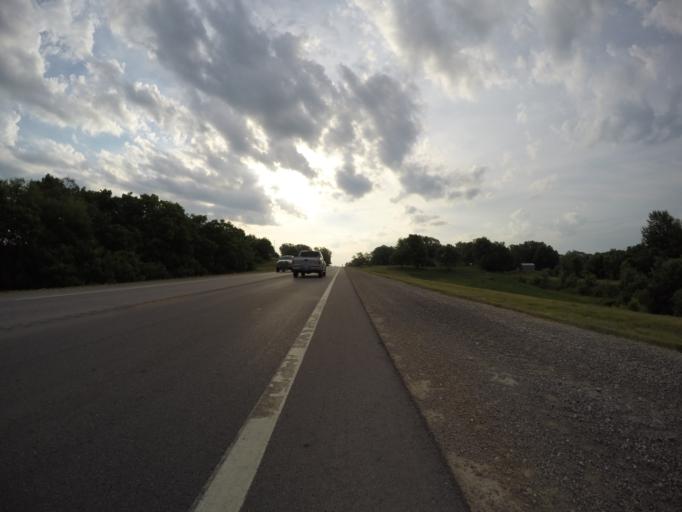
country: US
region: Kansas
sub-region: Doniphan County
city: Troy
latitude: 39.7926
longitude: -95.0701
